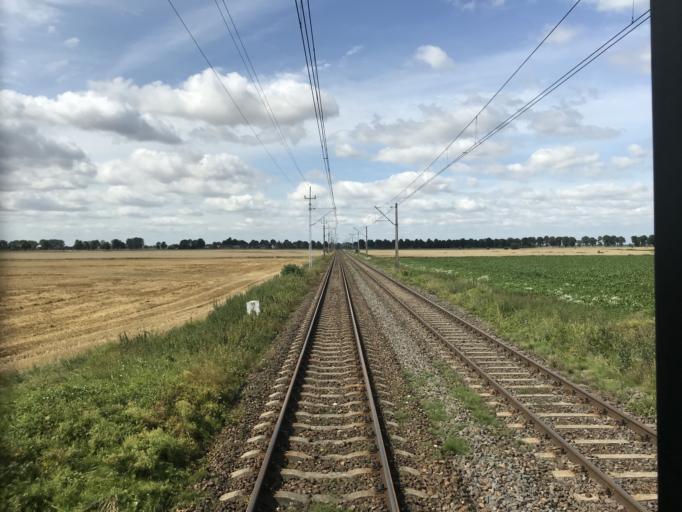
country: PL
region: Pomeranian Voivodeship
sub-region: Powiat malborski
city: Stare Pole
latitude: 54.0647
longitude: 19.2417
